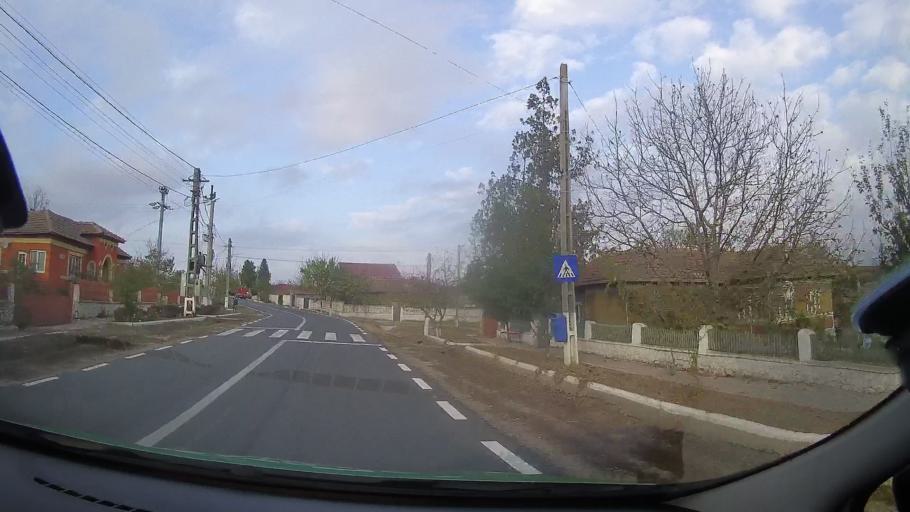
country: RO
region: Constanta
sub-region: Comuna Mircea Voda
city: Mircea Voda
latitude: 44.2825
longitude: 28.1774
